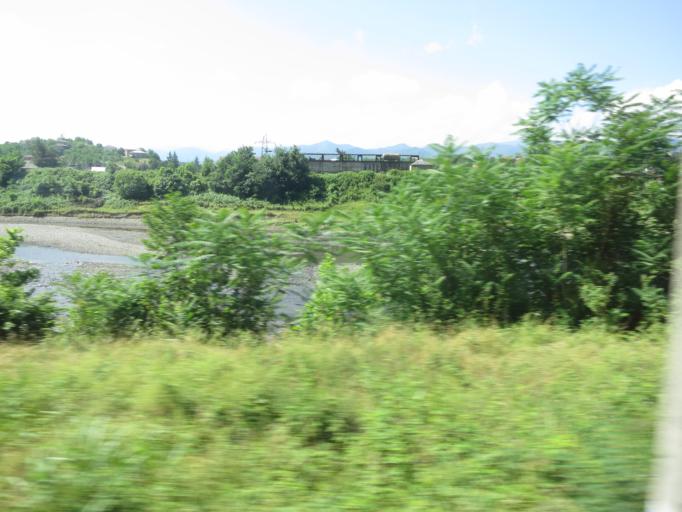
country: GE
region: Imereti
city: Zestap'oni
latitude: 42.1040
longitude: 43.0699
